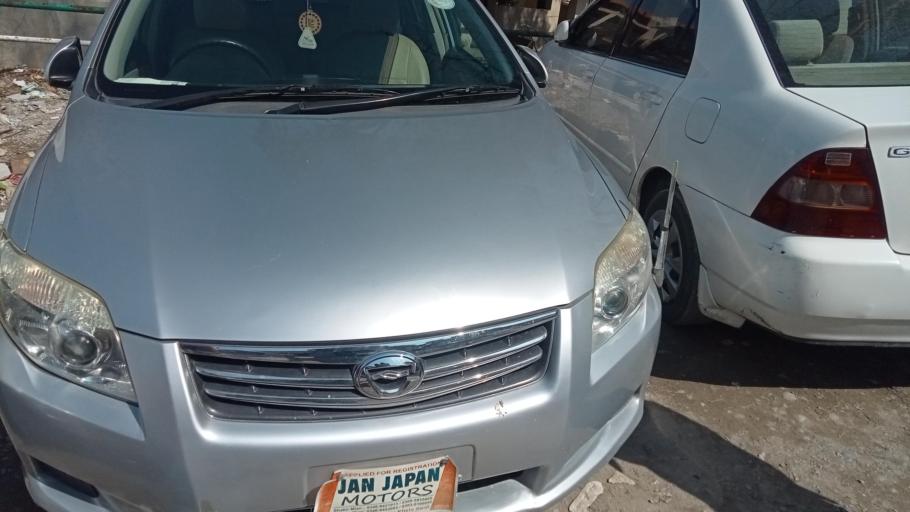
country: PK
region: Khyber Pakhtunkhwa
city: Saidu Sharif
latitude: 34.7591
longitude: 72.3588
